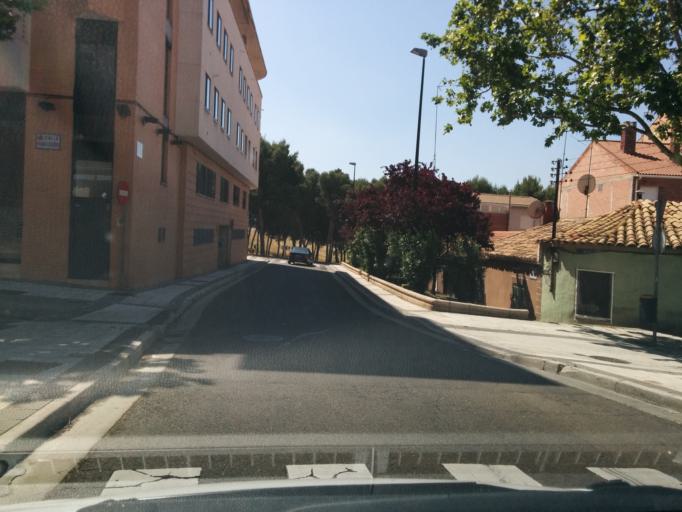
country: ES
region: Aragon
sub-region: Provincia de Zaragoza
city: Zaragoza
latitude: 41.6260
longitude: -0.8745
